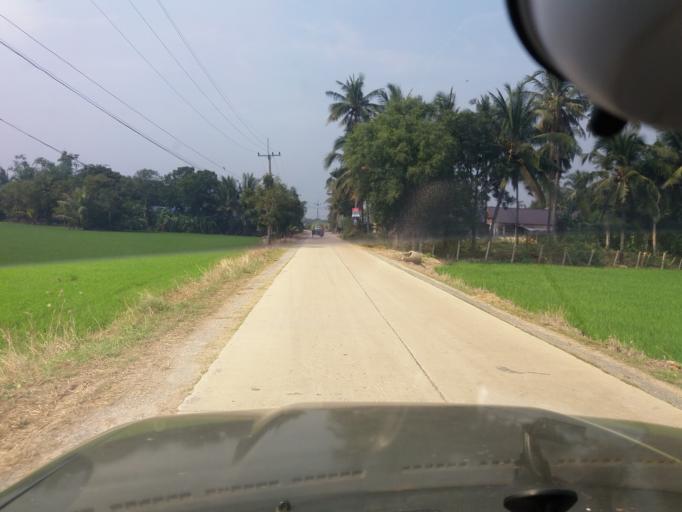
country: TH
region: Suphan Buri
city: Doem Bang Nang Buat
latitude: 14.8932
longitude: 100.1917
